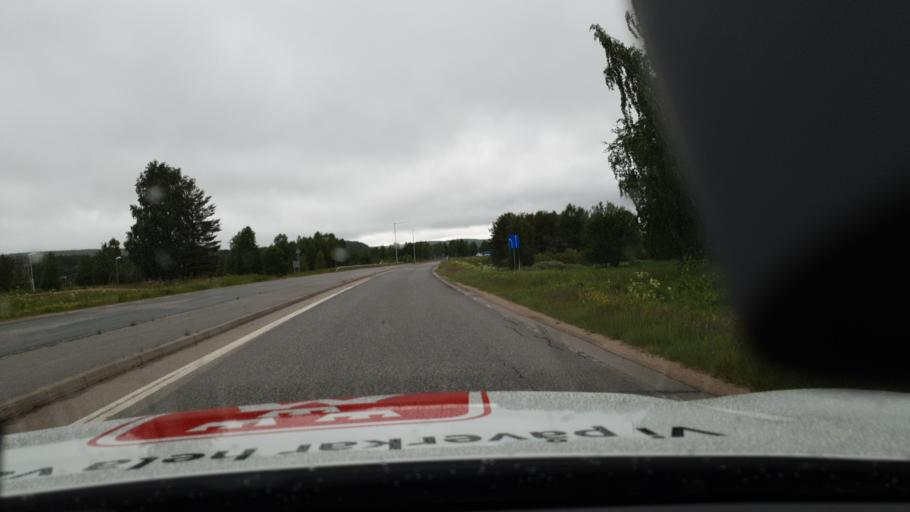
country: SE
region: Norrbotten
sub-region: Overtornea Kommun
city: OEvertornea
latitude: 66.3951
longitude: 23.6281
